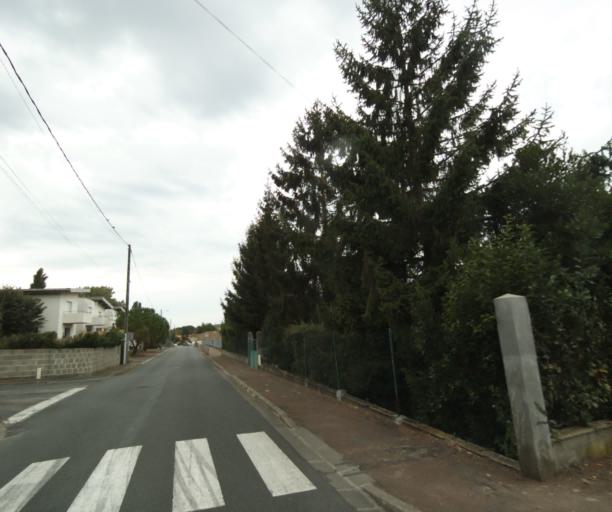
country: FR
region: Poitou-Charentes
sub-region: Departement de la Charente-Maritime
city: Tonnay-Charente
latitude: 45.9467
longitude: -0.8891
